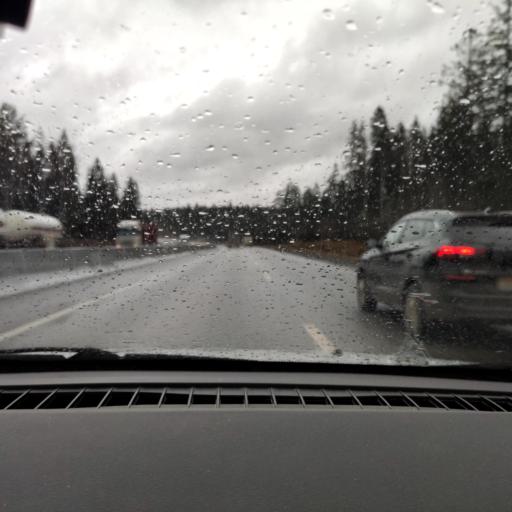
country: RU
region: Perm
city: Ferma
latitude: 57.9672
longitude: 56.4009
